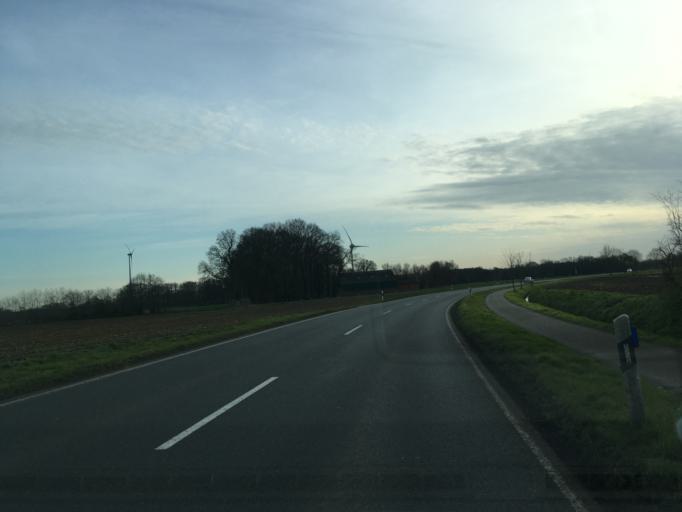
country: DE
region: North Rhine-Westphalia
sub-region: Regierungsbezirk Munster
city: Gescher
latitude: 52.0059
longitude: 7.0364
